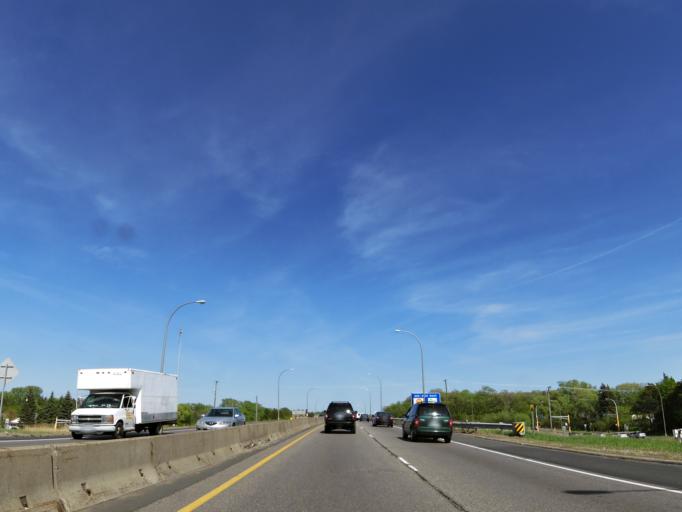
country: US
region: Minnesota
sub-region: Ramsey County
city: Roseville
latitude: 45.0104
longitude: -93.1486
